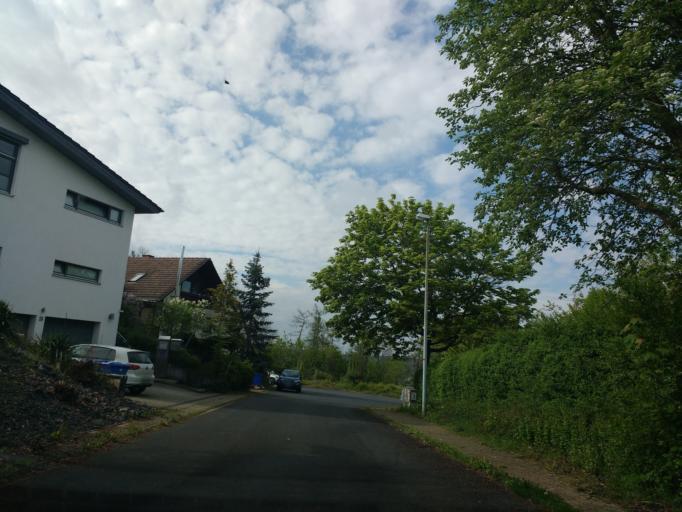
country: DE
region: Lower Saxony
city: Gemeinde Friedland
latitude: 51.4155
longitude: 9.9123
